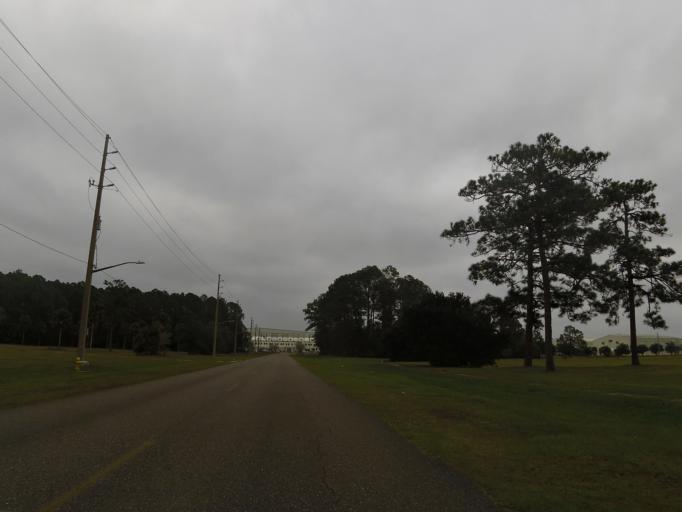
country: US
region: Florida
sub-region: Duval County
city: Baldwin
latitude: 30.2314
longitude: -81.8861
